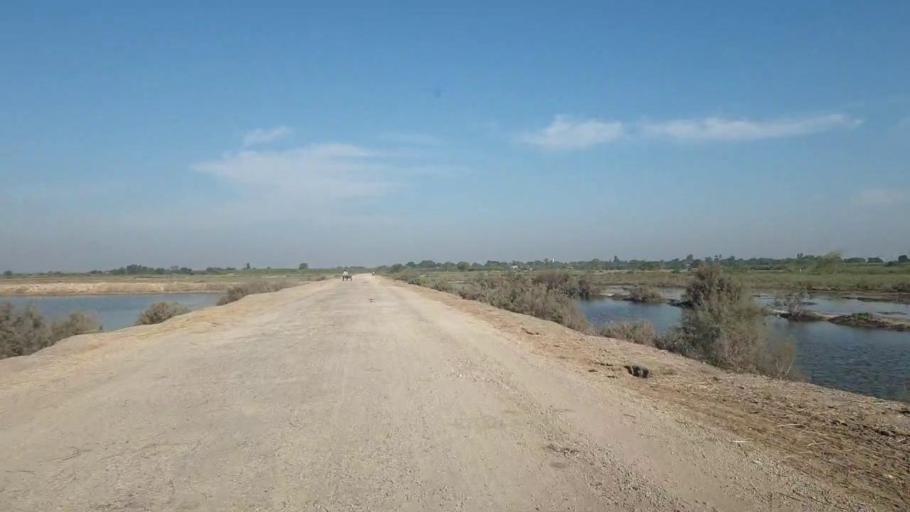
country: PK
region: Sindh
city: Talhar
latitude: 24.9191
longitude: 68.8016
